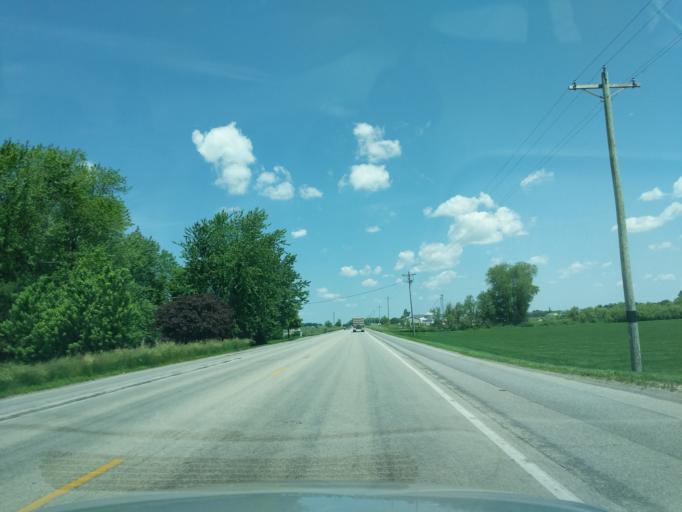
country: US
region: Indiana
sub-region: LaGrange County
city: Topeka
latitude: 41.6015
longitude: -85.5789
